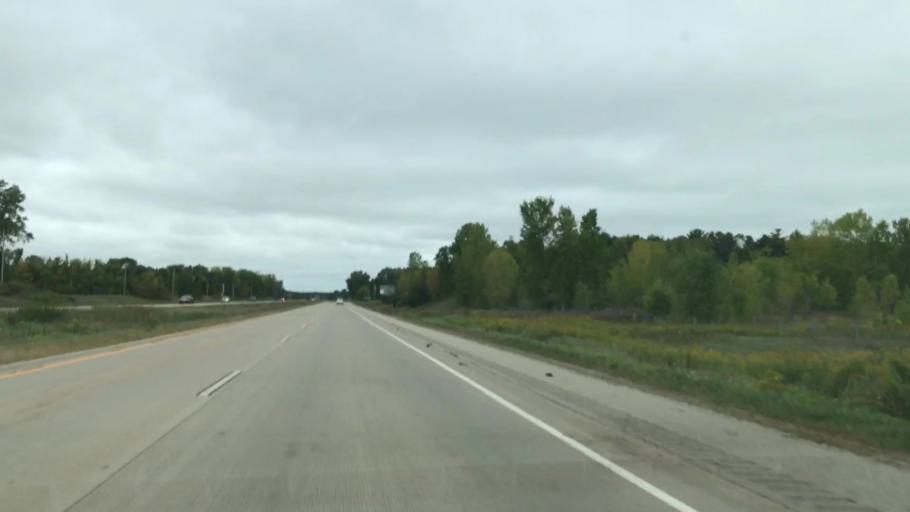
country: US
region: Wisconsin
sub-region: Oconto County
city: Oconto
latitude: 44.9820
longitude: -87.8636
